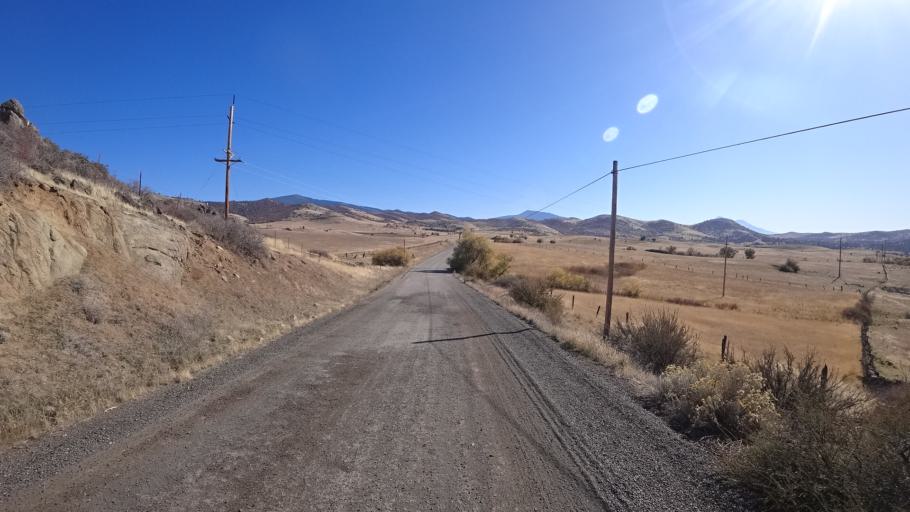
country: US
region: California
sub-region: Siskiyou County
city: Montague
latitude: 41.8311
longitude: -122.3719
